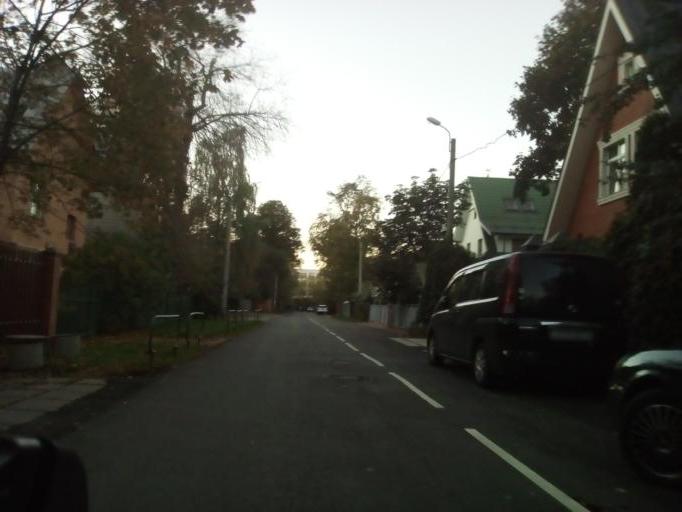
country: RU
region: Moscow
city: Sokol
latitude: 55.8038
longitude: 37.5028
